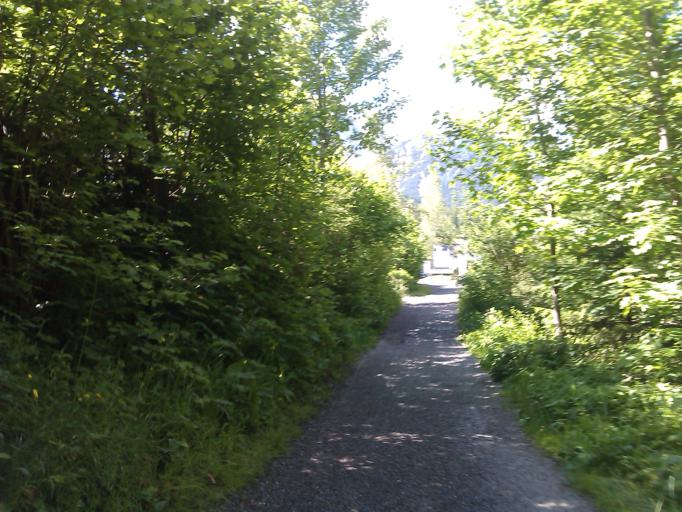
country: AT
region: Tyrol
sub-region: Politischer Bezirk Reutte
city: Biberwier
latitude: 47.3752
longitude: 10.8916
